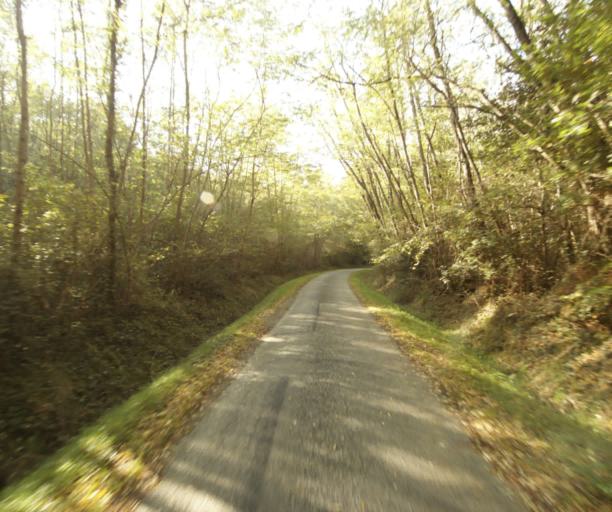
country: FR
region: Midi-Pyrenees
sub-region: Departement du Tarn-et-Garonne
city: Nohic
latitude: 43.9248
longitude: 1.4455
